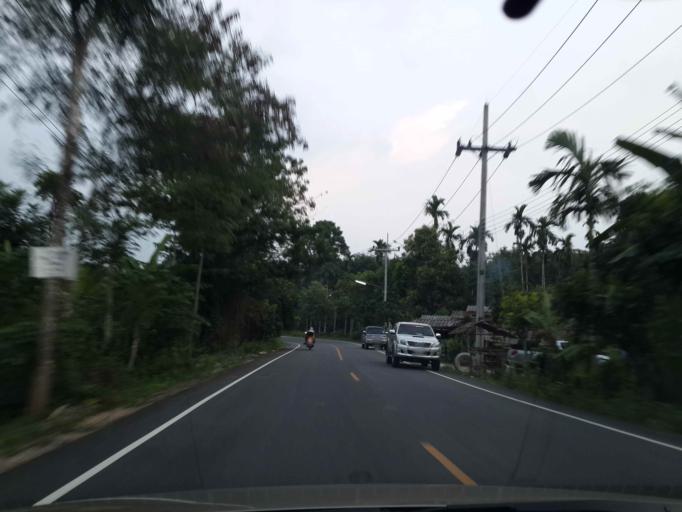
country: TH
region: Narathiwat
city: Rueso
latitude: 6.3480
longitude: 101.4774
